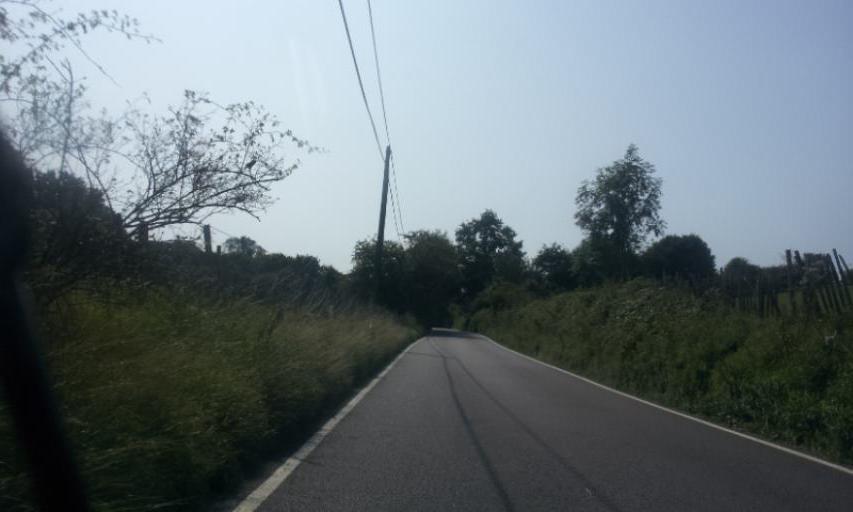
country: GB
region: England
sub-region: Kent
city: Gillingham
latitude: 51.3450
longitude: 0.5647
